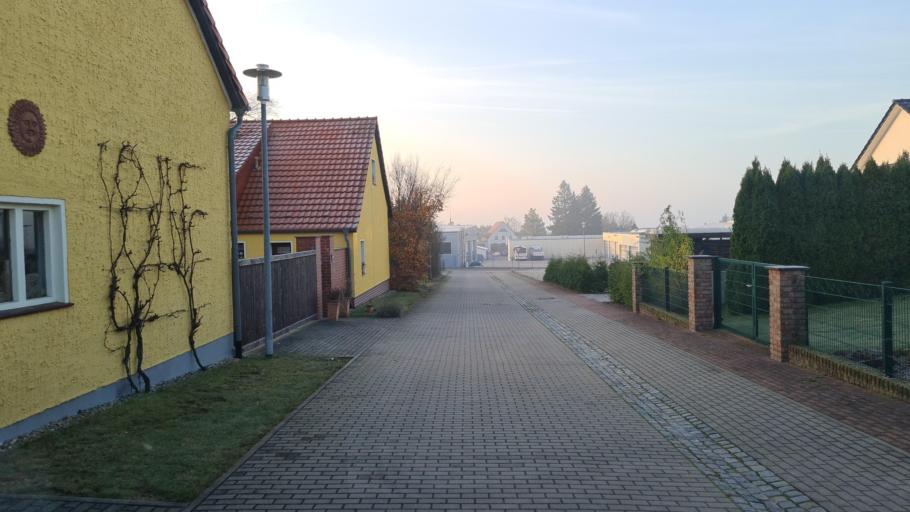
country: DE
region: Saxony-Anhalt
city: Jessen
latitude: 51.7981
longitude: 12.9733
